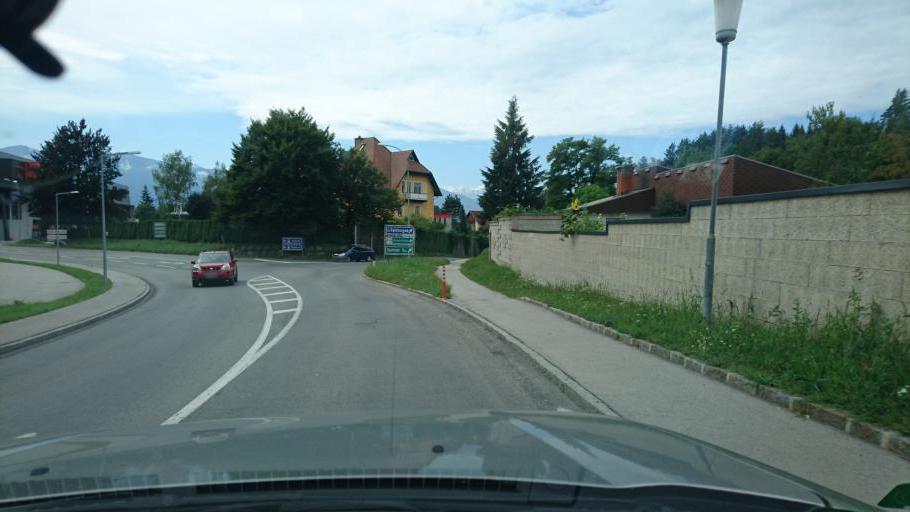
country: AT
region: Carinthia
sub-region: Villach Stadt
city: Villach
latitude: 46.6293
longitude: 13.8782
